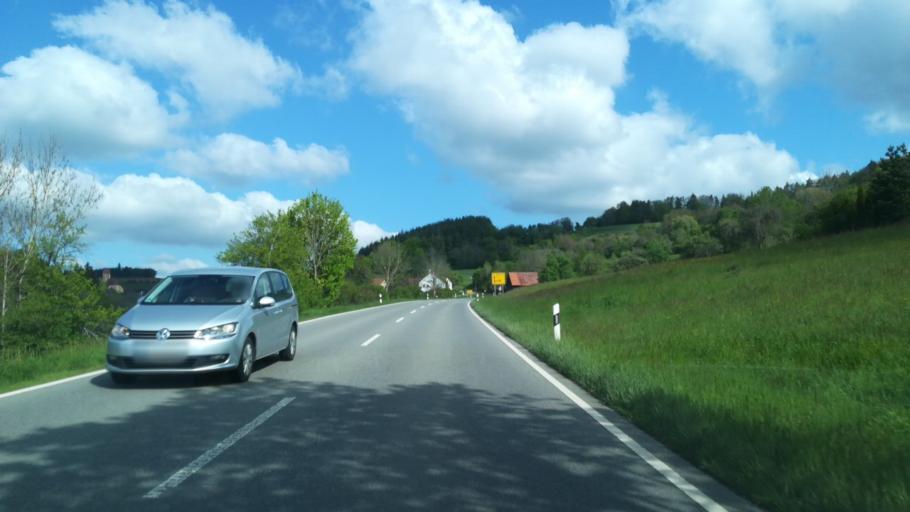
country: DE
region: Baden-Wuerttemberg
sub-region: Freiburg Region
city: Tengen
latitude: 47.8105
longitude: 8.6919
